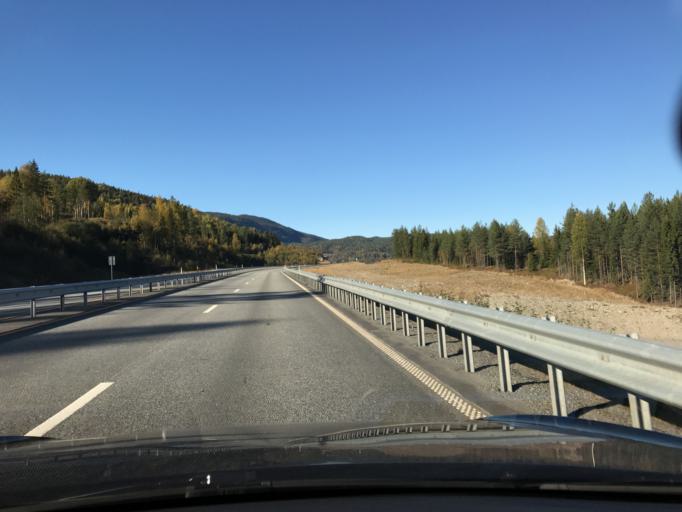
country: NO
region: Buskerud
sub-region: Krodsherad
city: Noresund
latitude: 60.2713
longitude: 9.7785
